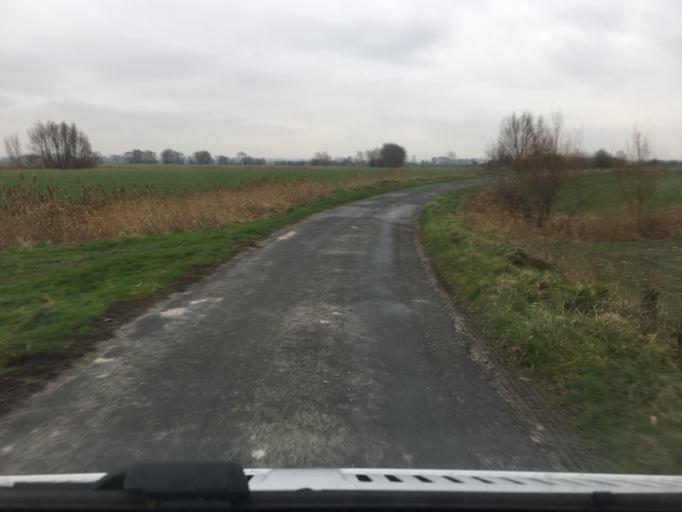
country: FR
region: Picardie
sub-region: Departement de la Somme
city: Pende
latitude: 50.1938
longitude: 1.5489
